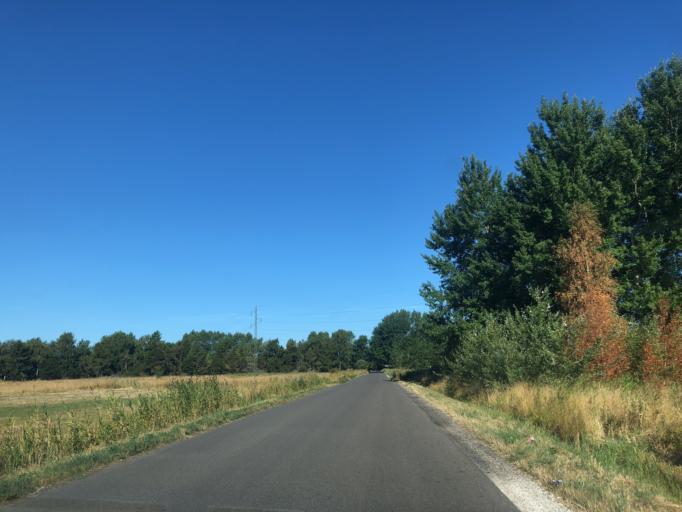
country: DK
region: Zealand
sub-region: Slagelse Kommune
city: Forlev
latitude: 55.3760
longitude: 11.2286
